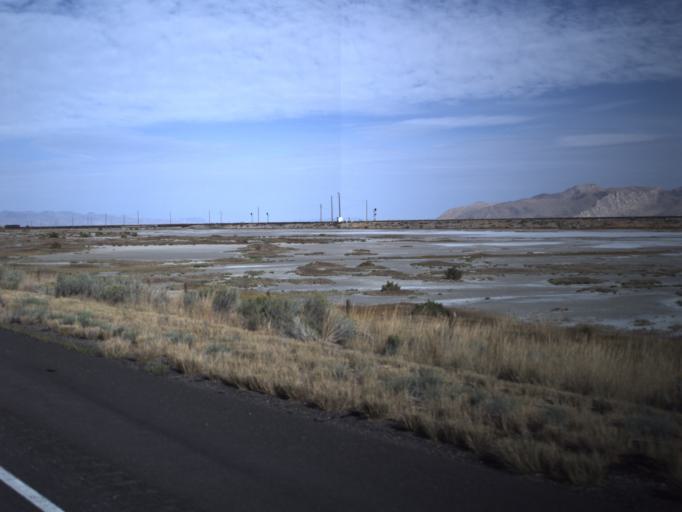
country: US
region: Utah
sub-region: Tooele County
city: Grantsville
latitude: 40.6830
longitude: -112.4328
